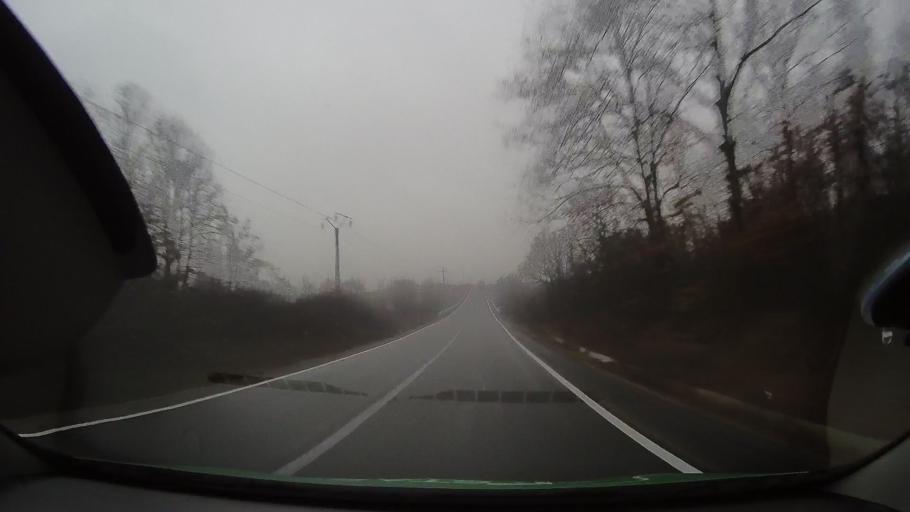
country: RO
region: Bihor
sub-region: Comuna Olcea
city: Olcea
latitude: 46.6950
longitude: 21.9649
